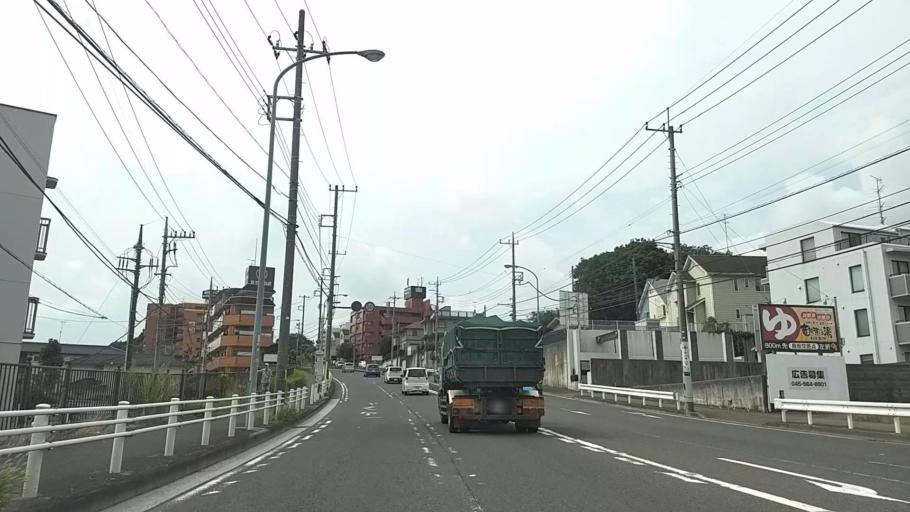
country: JP
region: Kanagawa
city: Minami-rinkan
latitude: 35.5073
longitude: 139.5435
